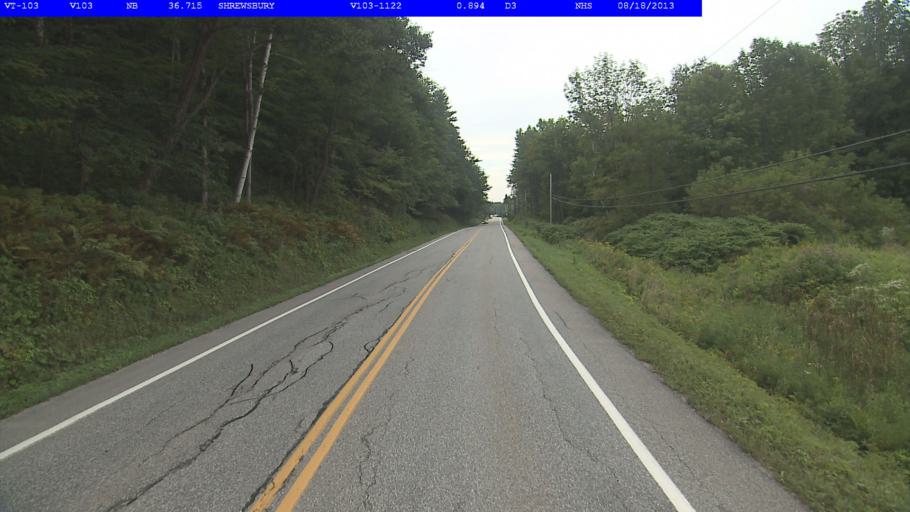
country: US
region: Vermont
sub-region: Rutland County
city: Rutland
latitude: 43.4858
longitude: -72.8955
